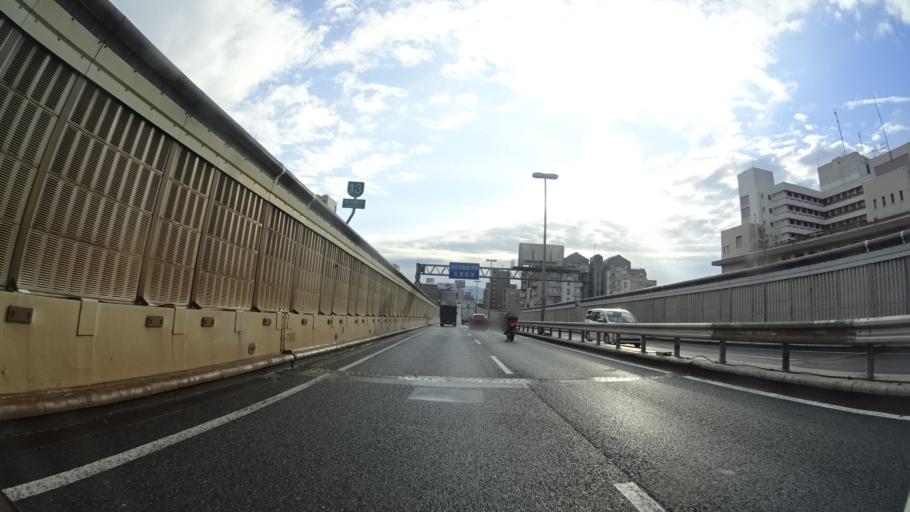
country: JP
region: Osaka
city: Osaka-shi
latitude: 34.6814
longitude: 135.5353
